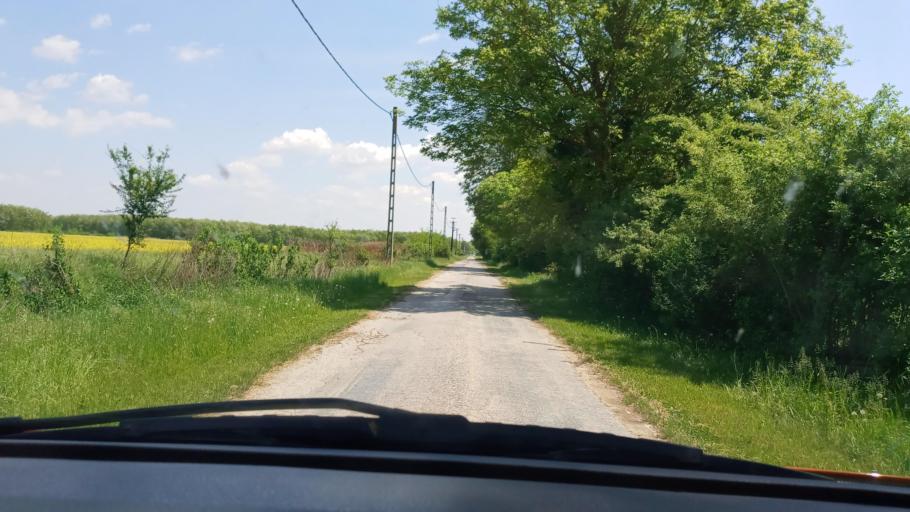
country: HU
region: Baranya
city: Siklos
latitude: 45.7708
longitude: 18.2782
